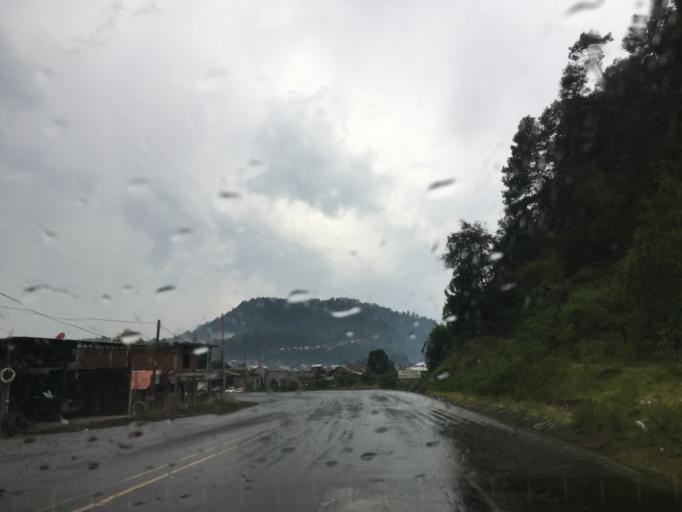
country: MX
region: Michoacan
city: Angahuan
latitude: 19.5536
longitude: -102.2204
